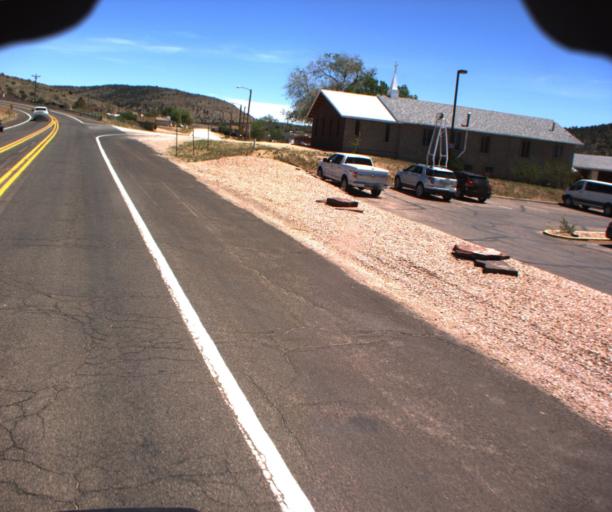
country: US
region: Arizona
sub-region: Mohave County
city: Peach Springs
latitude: 35.5293
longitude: -113.4242
